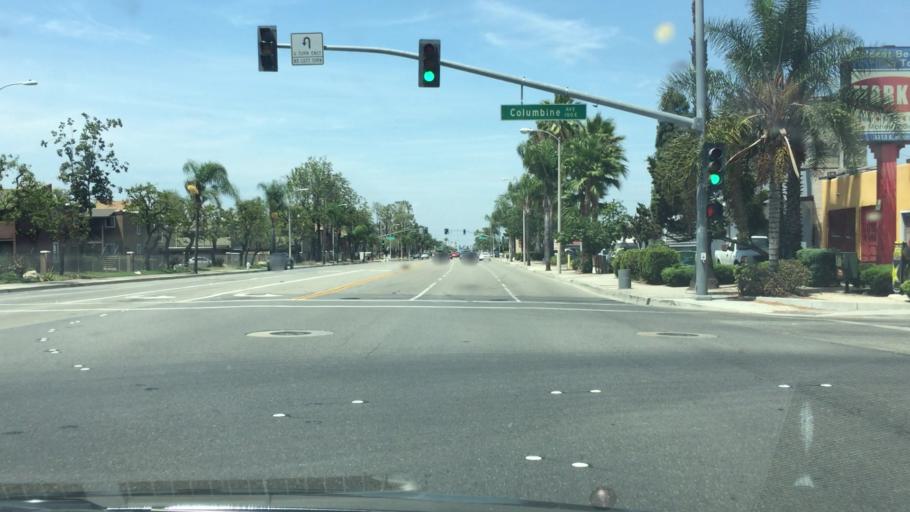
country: US
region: California
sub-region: Orange County
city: Santa Ana
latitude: 33.7033
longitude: -117.8679
